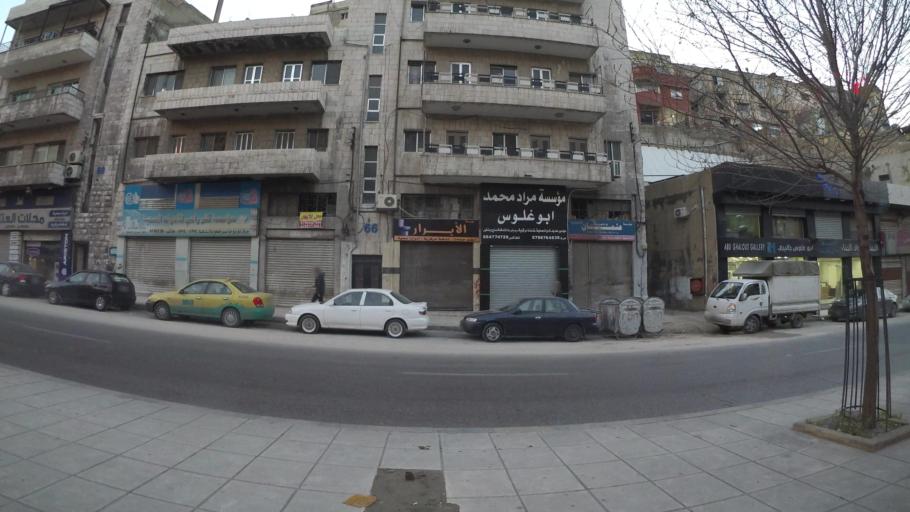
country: JO
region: Amman
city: Amman
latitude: 31.9394
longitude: 35.9233
